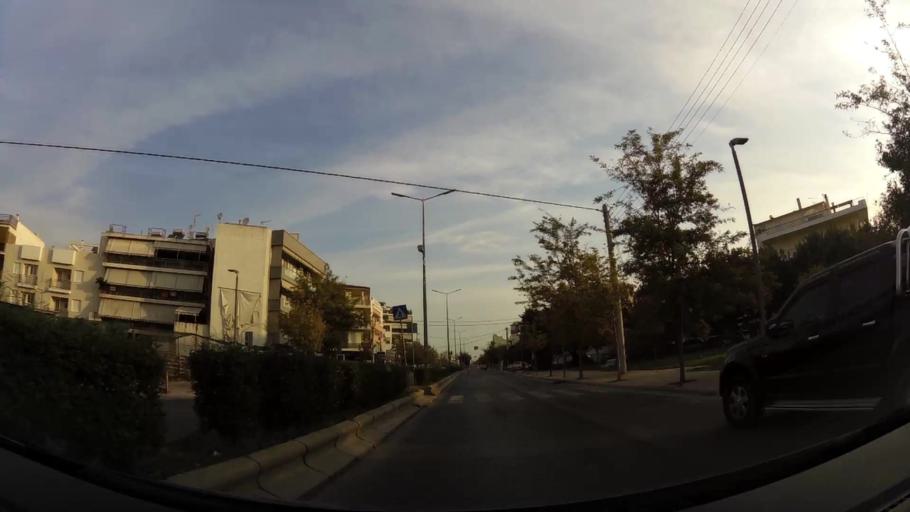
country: GR
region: Attica
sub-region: Nomarchia Athinas
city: Ilion
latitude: 38.0323
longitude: 23.7018
